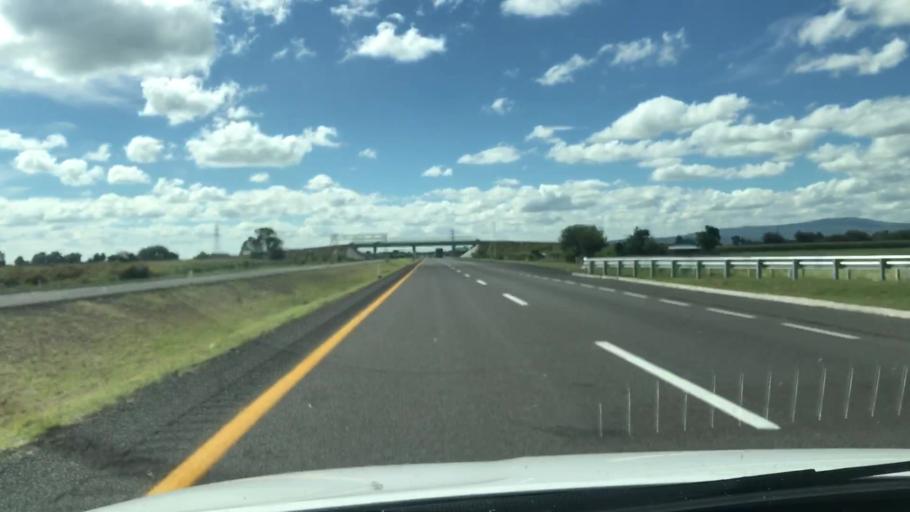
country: MX
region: Guanajuato
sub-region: Silao de la Victoria
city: La Aldea
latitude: 20.9088
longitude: -101.4908
